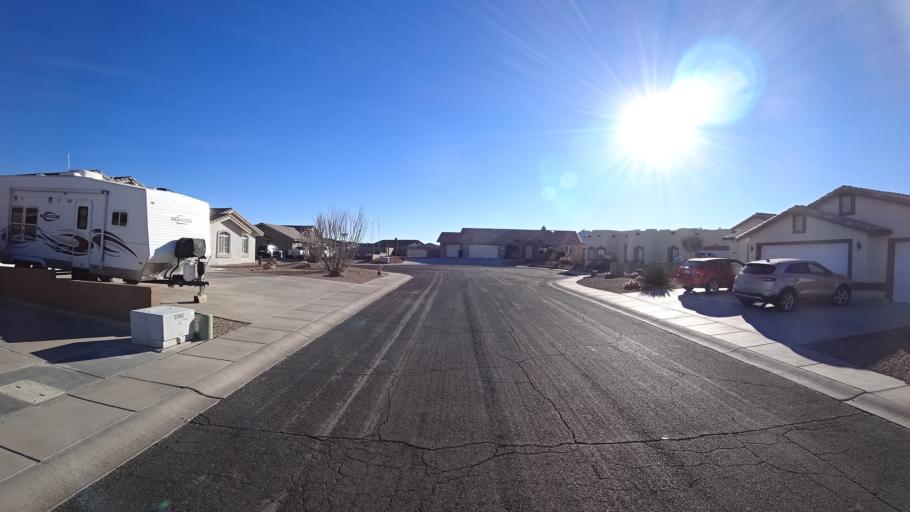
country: US
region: Arizona
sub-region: Mohave County
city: Kingman
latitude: 35.1926
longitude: -114.0036
